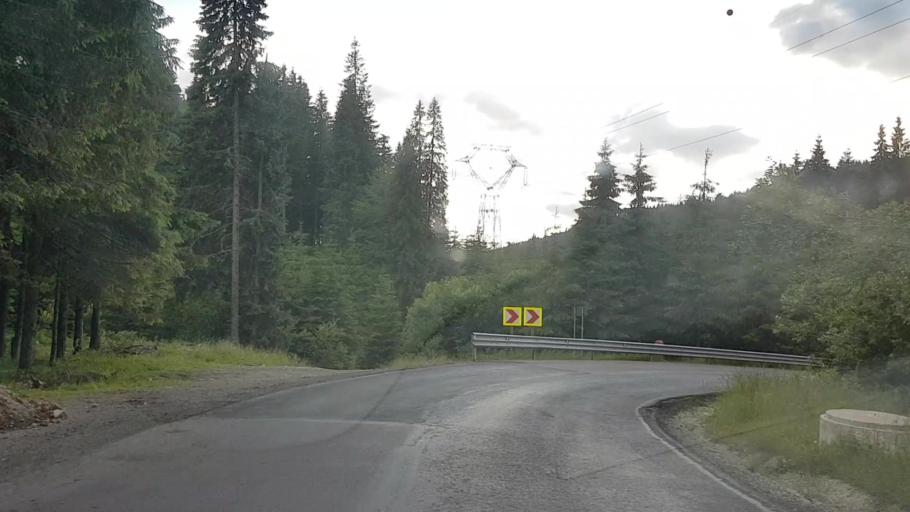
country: RO
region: Harghita
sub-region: Comuna Varsag
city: Varsag
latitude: 46.6422
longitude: 25.2829
